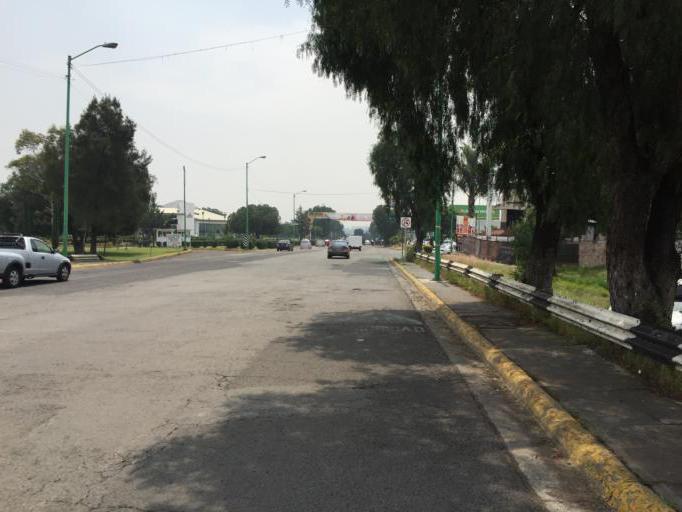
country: MX
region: Mexico
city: Cuautitlan Izcalli
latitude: 19.6558
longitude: -99.2089
